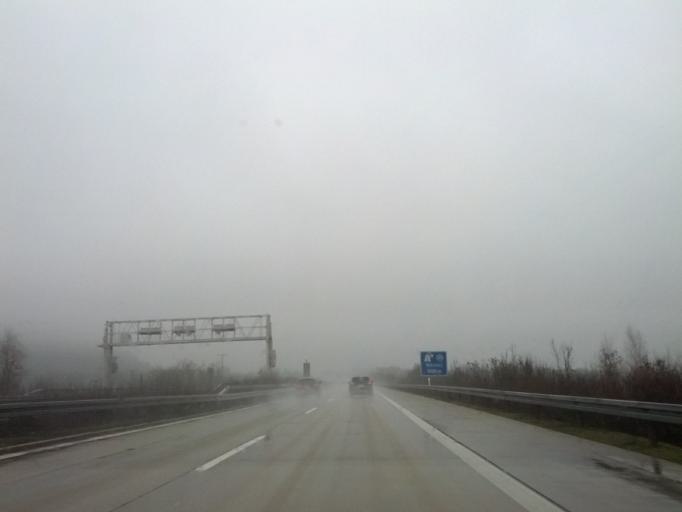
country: DE
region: Bavaria
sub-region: Regierungsbezirk Mittelfranken
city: Schillingsfurst
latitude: 49.2516
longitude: 10.2248
